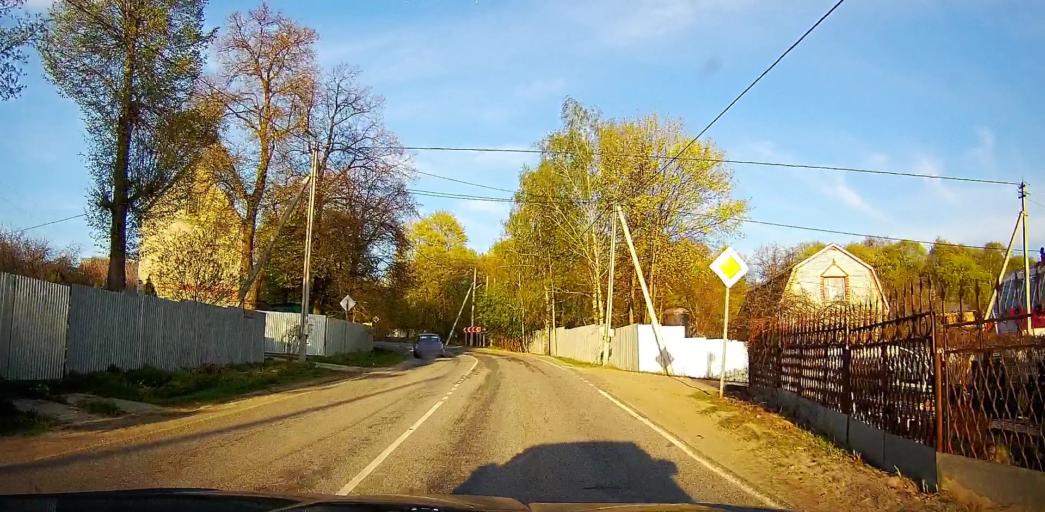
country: RU
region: Moskovskaya
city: Meshcherino
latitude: 55.2435
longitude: 38.3146
